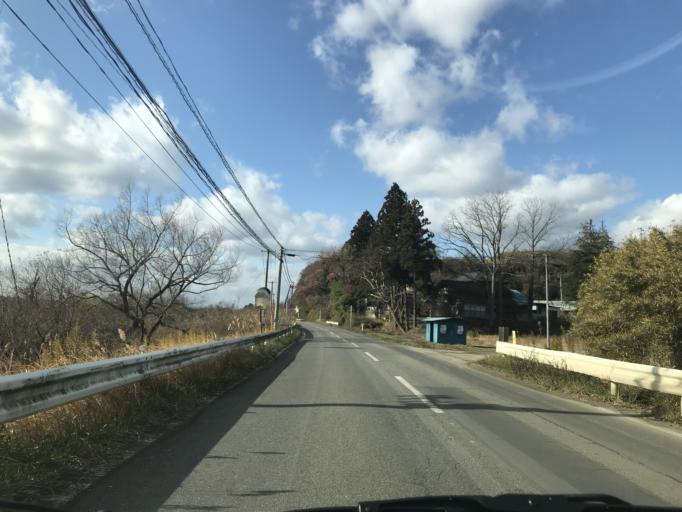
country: JP
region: Miyagi
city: Kogota
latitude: 38.7265
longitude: 141.0806
